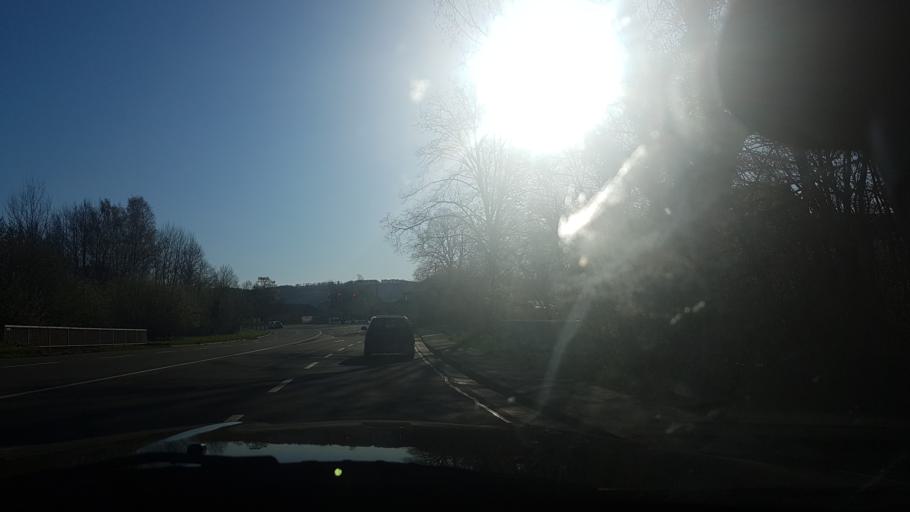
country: DE
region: Lower Saxony
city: Springe
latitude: 52.1734
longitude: 9.5143
